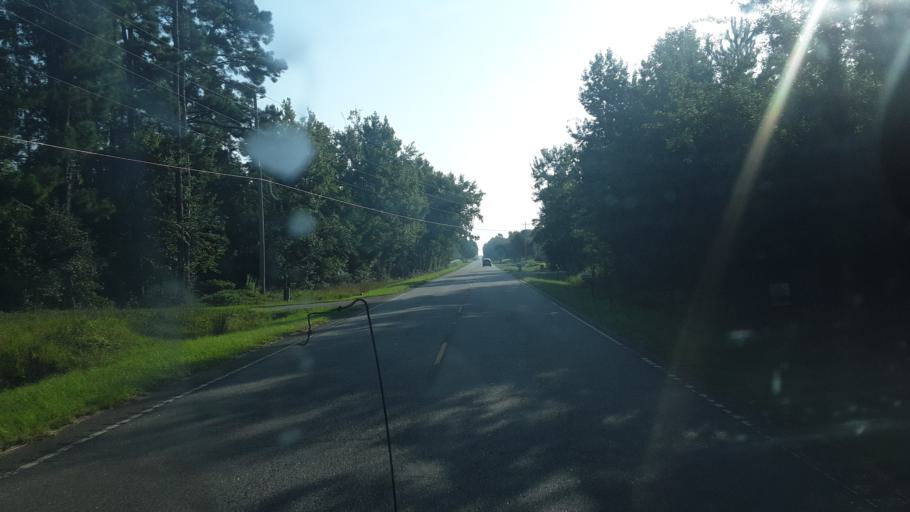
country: US
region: South Carolina
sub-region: Horry County
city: Forestbrook
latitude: 33.8402
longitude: -78.8670
